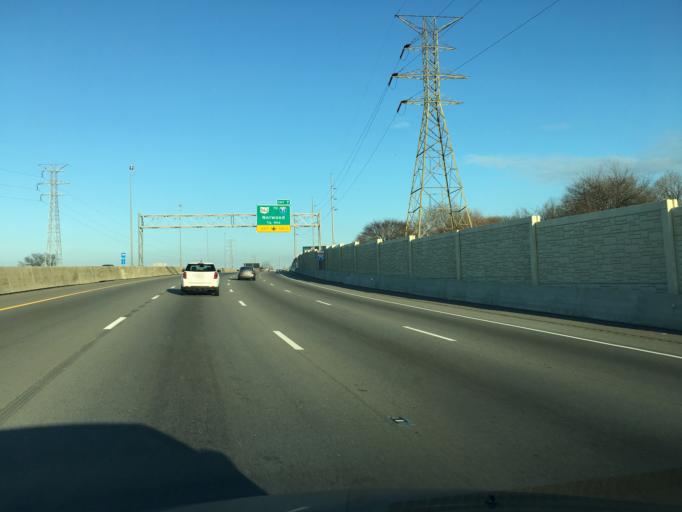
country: US
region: Ohio
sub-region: Hamilton County
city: Saint Bernard
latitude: 39.1696
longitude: -84.5032
